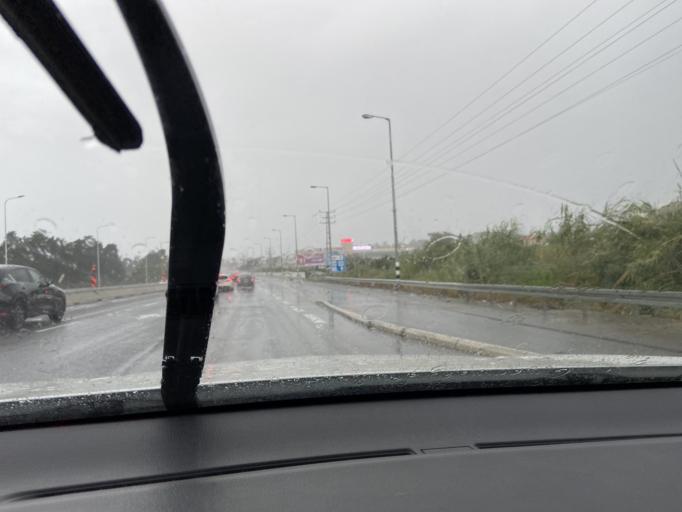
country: IL
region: Northern District
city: El Mazra`a
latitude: 32.9834
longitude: 35.0949
